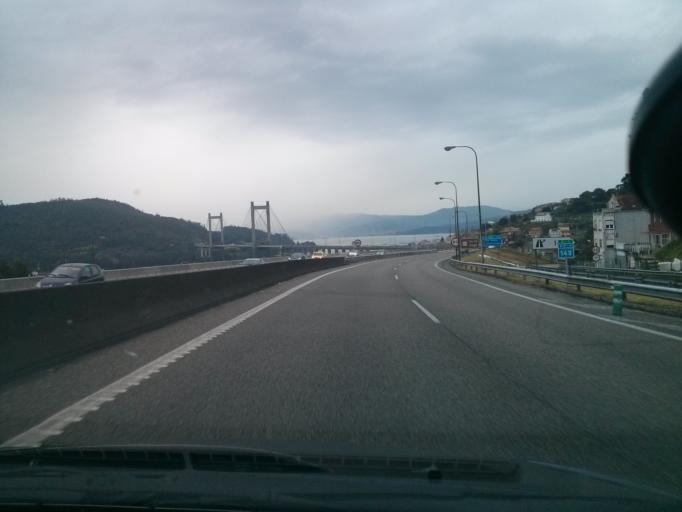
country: ES
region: Galicia
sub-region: Provincia de Pontevedra
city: Redondela
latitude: 42.2773
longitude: -8.6653
